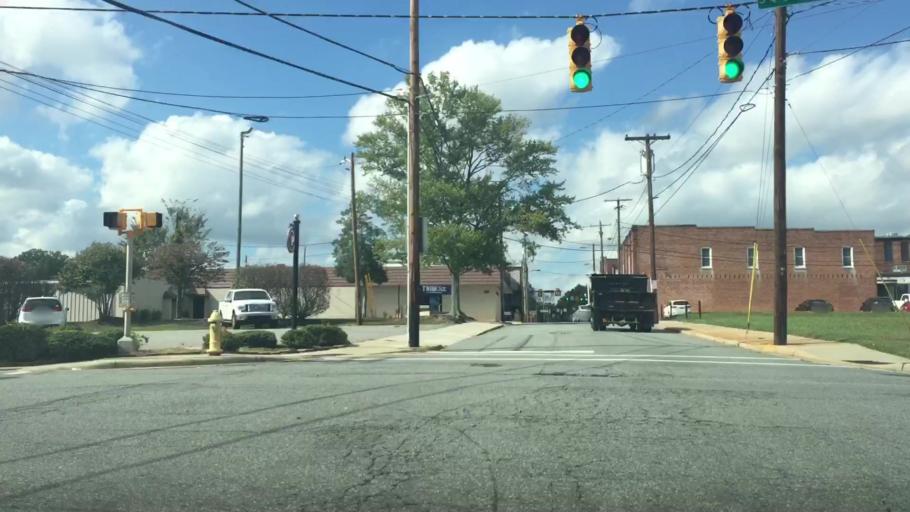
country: US
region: North Carolina
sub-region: Iredell County
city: Mooresville
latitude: 35.5815
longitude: -80.8116
